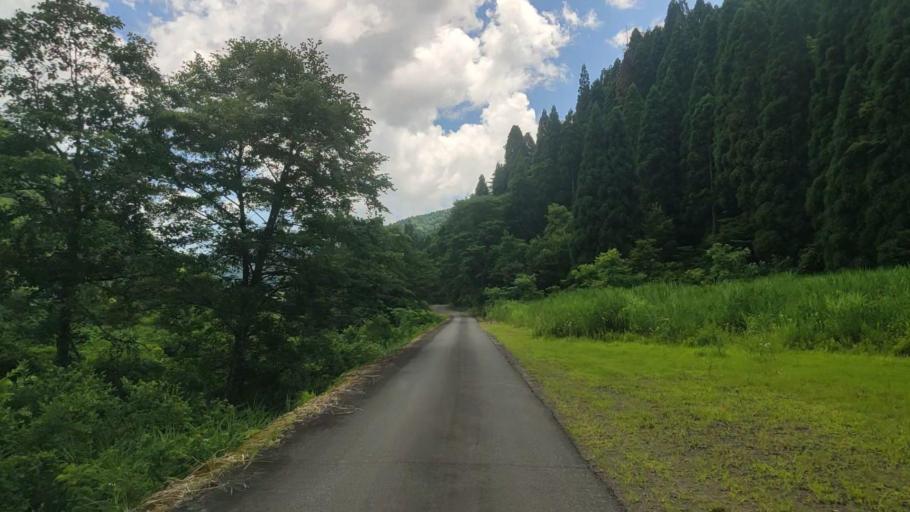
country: JP
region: Fukui
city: Ono
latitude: 35.8140
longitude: 136.4603
